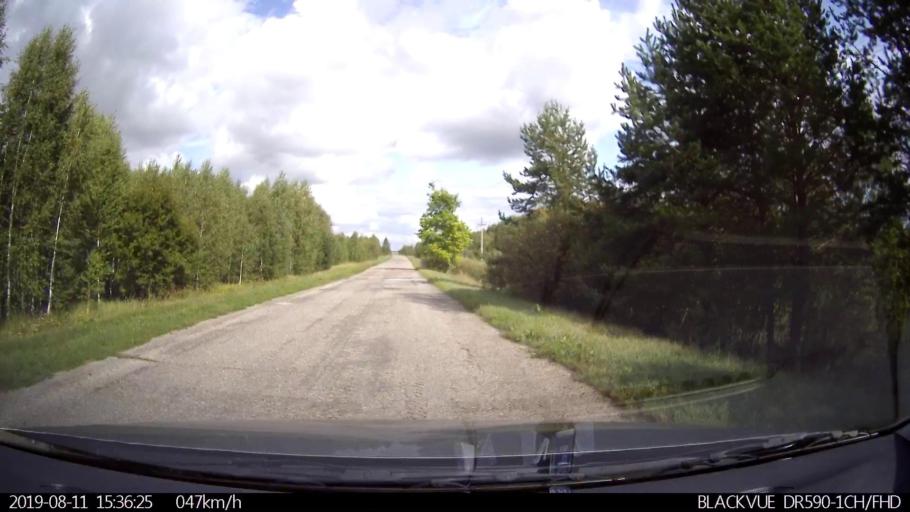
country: RU
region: Ulyanovsk
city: Ignatovka
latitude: 53.8594
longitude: 47.6201
